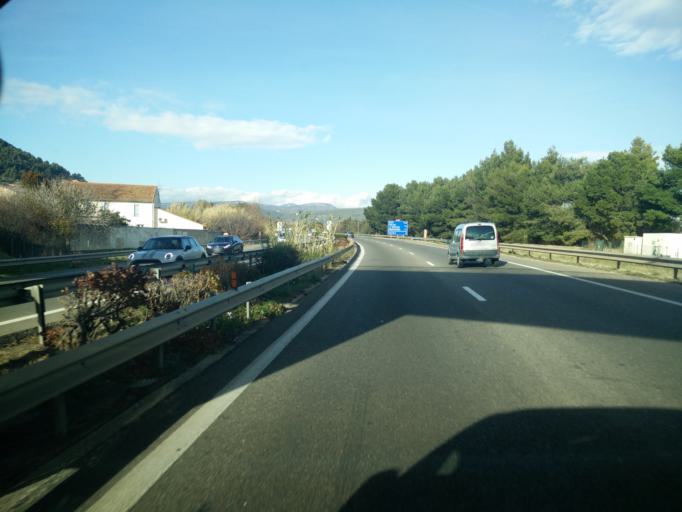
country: FR
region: Provence-Alpes-Cote d'Azur
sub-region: Departement du Var
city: La Farlede
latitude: 43.1655
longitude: 6.0517
